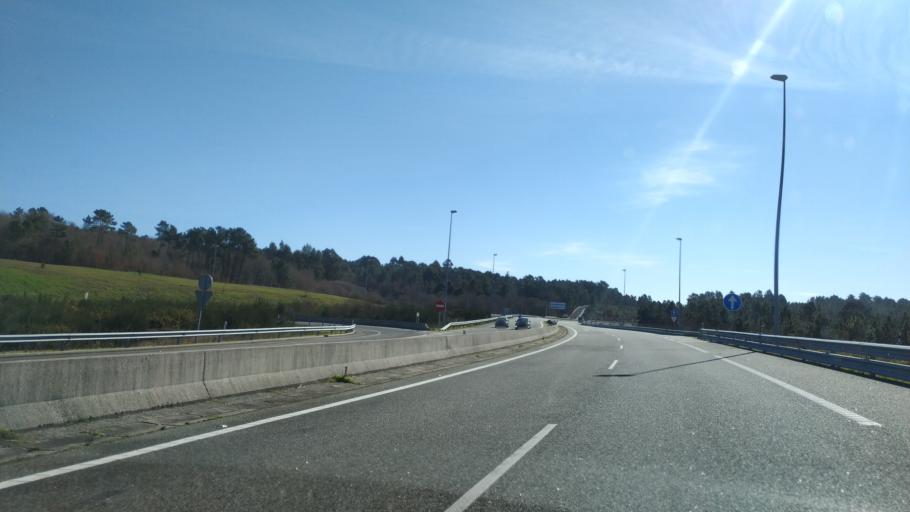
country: ES
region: Galicia
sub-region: Provincia de Ourense
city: Maside
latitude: 42.4493
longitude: -8.0234
